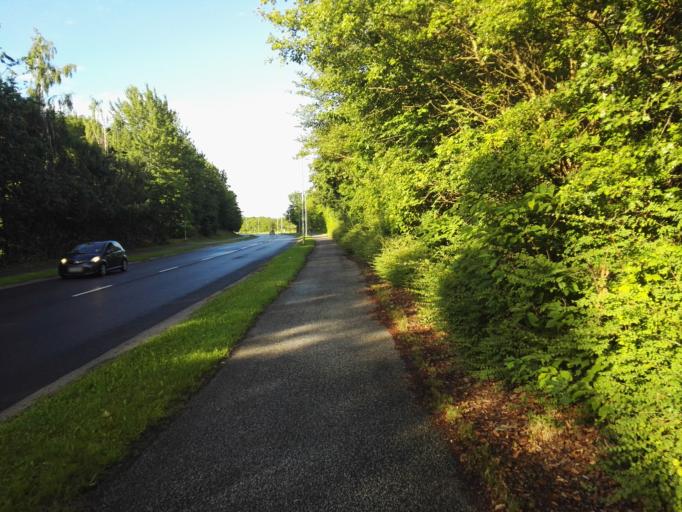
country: DK
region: Capital Region
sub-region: Egedal Kommune
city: Smorumnedre
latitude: 55.7379
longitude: 12.3126
